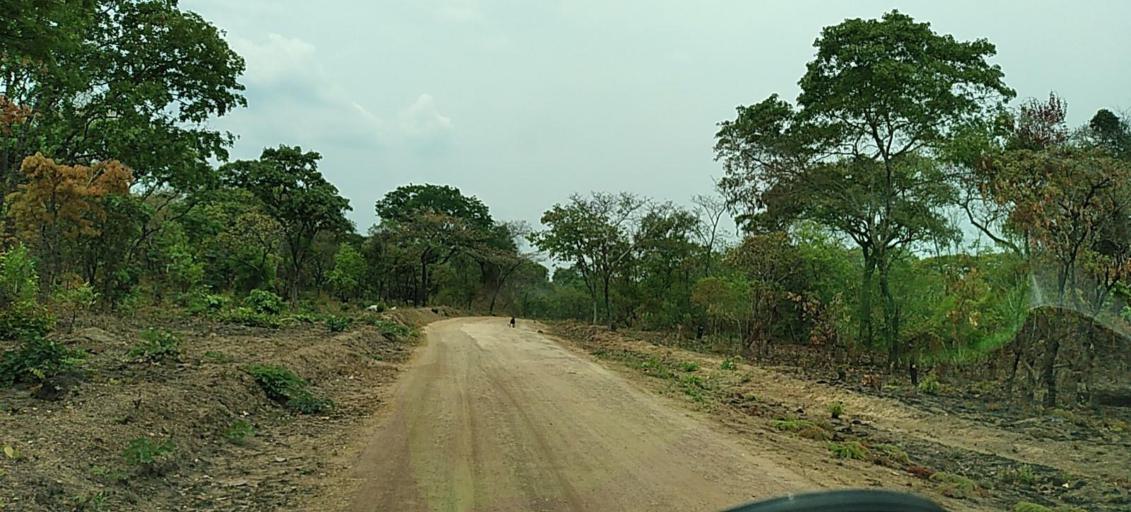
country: ZM
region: North-Western
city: Solwezi
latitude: -12.7834
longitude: 26.5186
